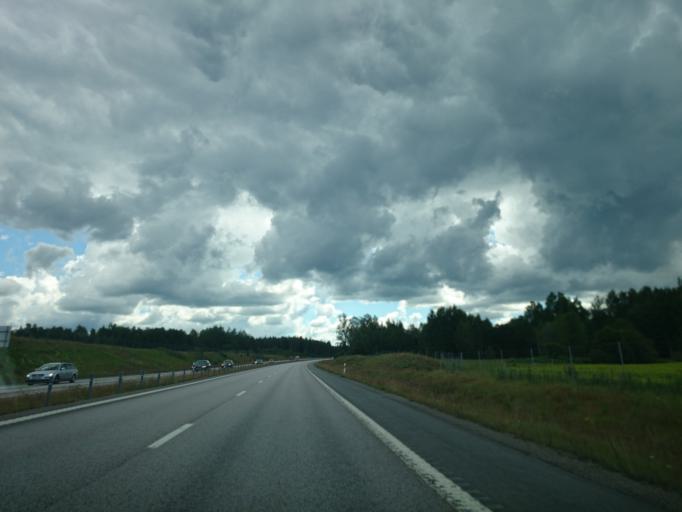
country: SE
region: Uppsala
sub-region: Tierps Kommun
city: Tierp
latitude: 60.3204
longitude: 17.5157
